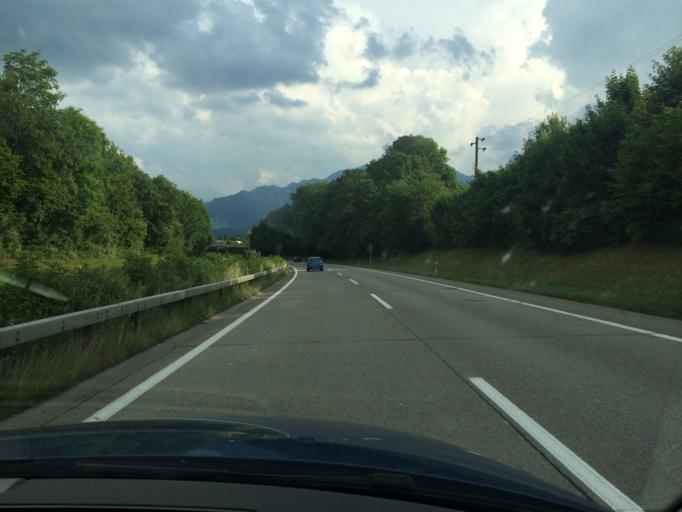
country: CH
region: Bern
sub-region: Thun District
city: Thierachern
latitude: 46.7651
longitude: 7.5938
